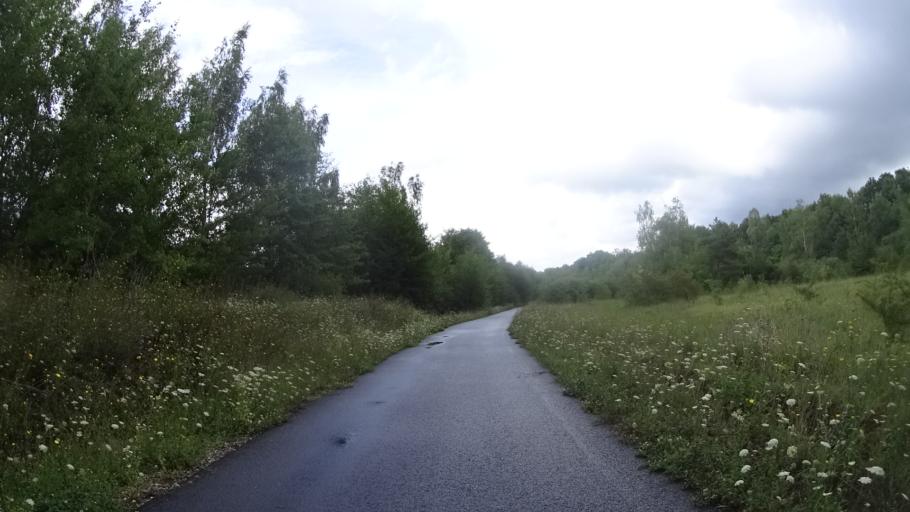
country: FR
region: Lorraine
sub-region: Departement de la Moselle
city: Lorquin
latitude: 48.6862
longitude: 6.8376
